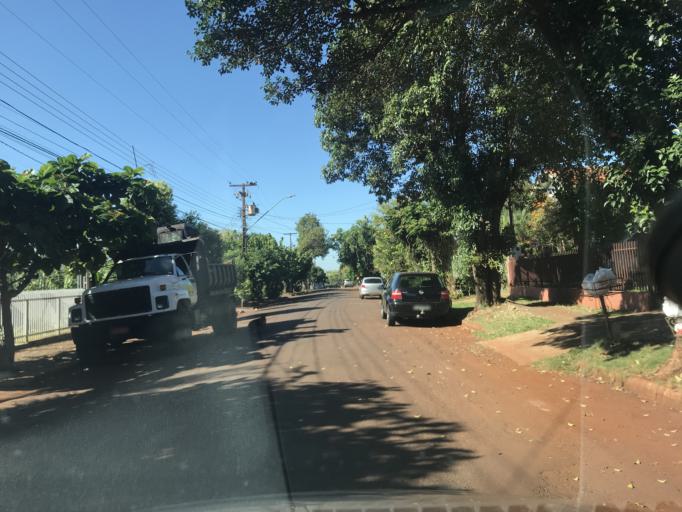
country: BR
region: Parana
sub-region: Palotina
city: Palotina
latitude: -24.2807
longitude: -53.8263
